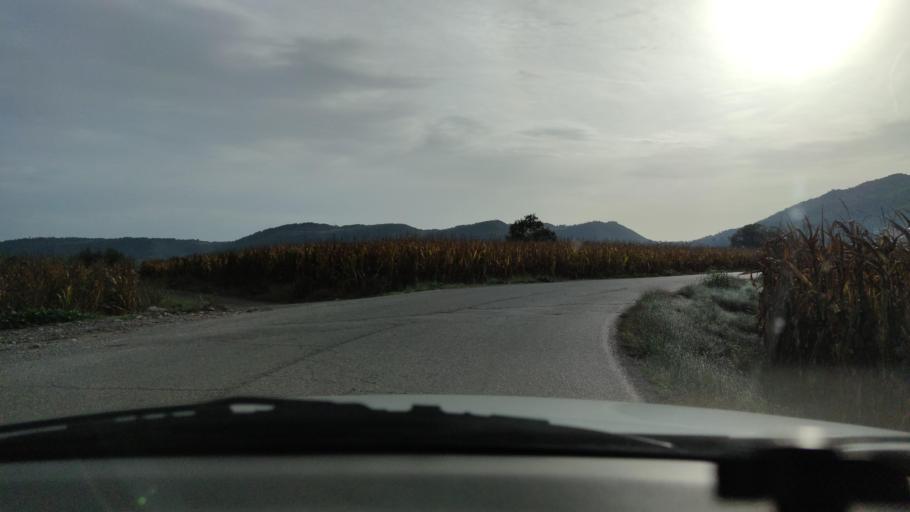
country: ES
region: Catalonia
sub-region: Provincia de Lleida
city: Artesa de Segre
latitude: 41.9015
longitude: 1.0445
